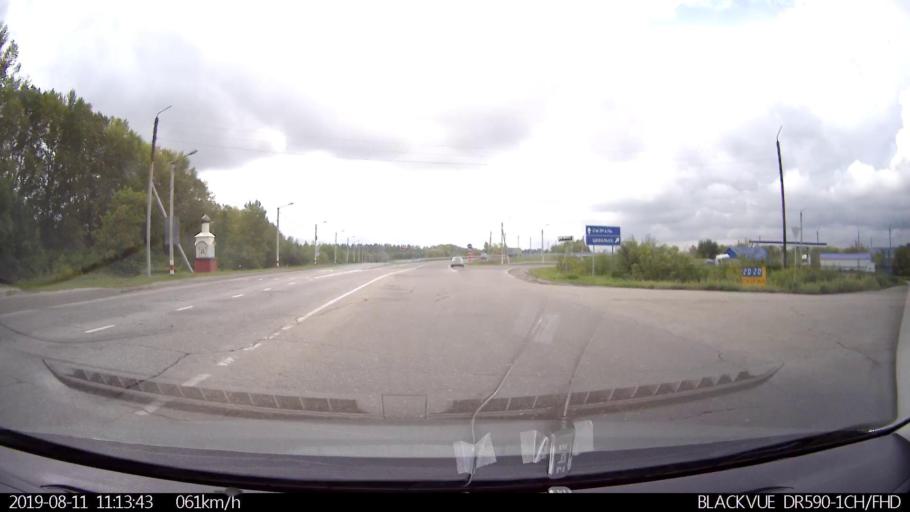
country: RU
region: Ulyanovsk
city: Novoul'yanovsk
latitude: 54.2133
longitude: 48.2974
